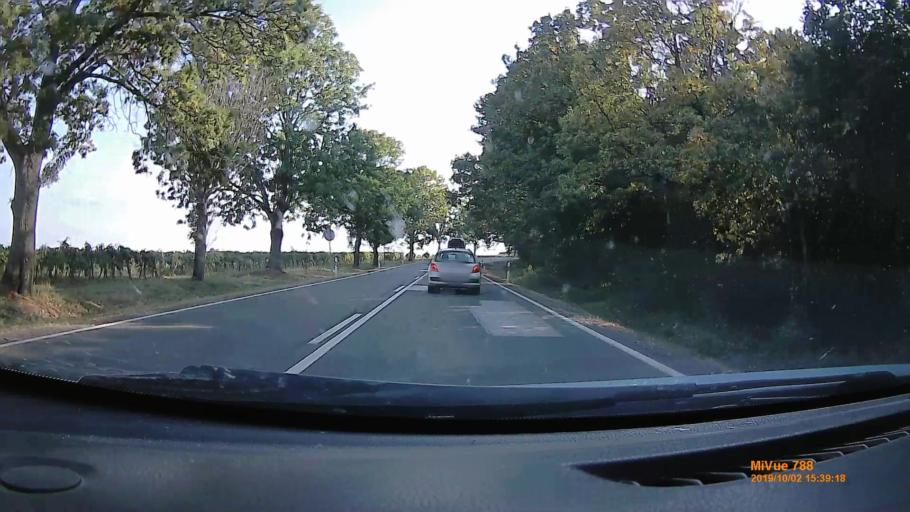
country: HU
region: Heves
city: Kerecsend
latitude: 47.8182
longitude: 20.3584
